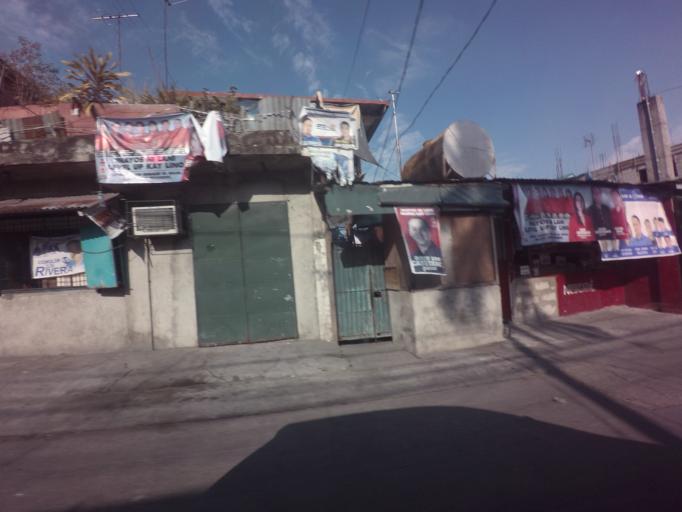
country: PH
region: Calabarzon
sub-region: Province of Rizal
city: Taguig
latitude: 14.4957
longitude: 121.0478
